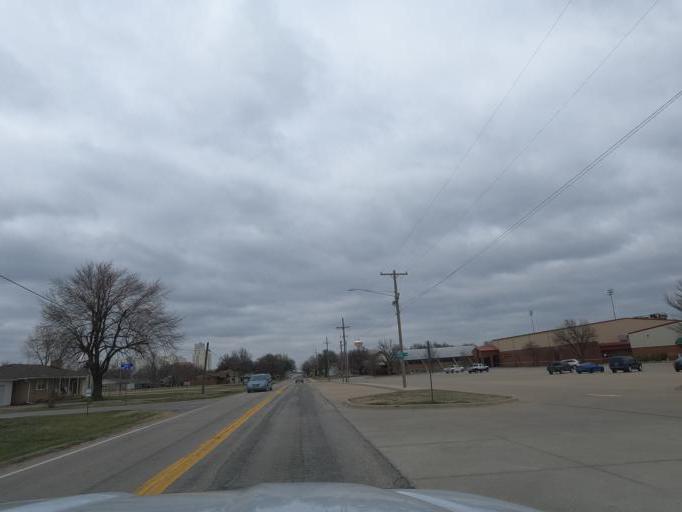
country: US
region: Kansas
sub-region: McPherson County
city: Inman
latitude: 38.2261
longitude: -97.7758
